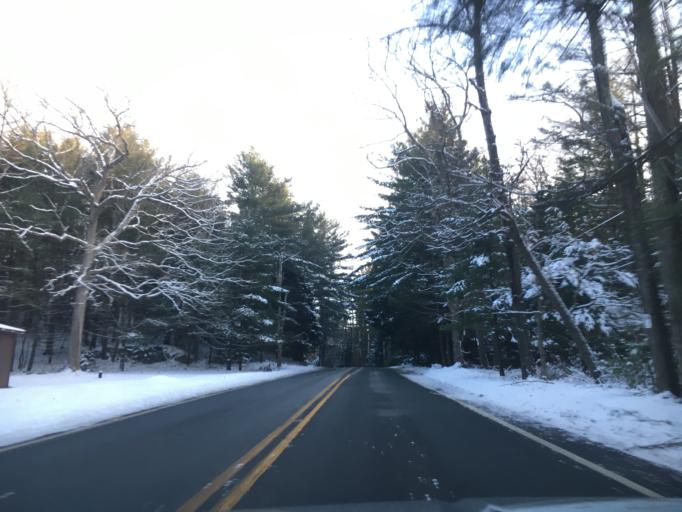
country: US
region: Pennsylvania
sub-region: Pike County
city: Hemlock Farms
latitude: 41.3237
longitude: -75.1198
